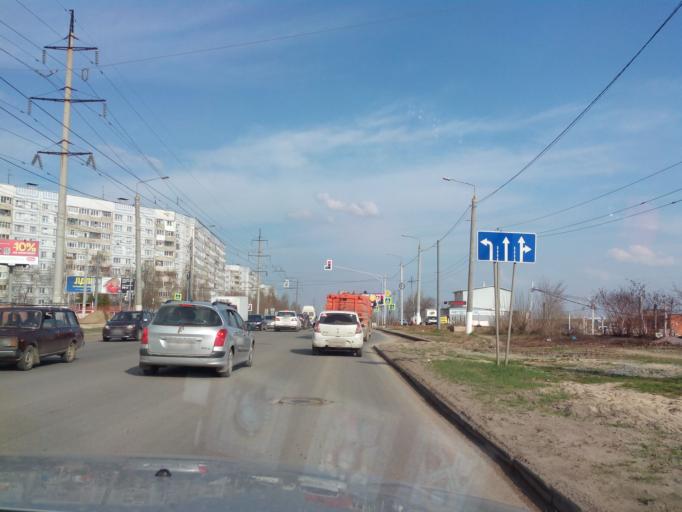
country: RU
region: Rjazan
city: Ryazan'
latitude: 54.6601
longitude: 39.6667
